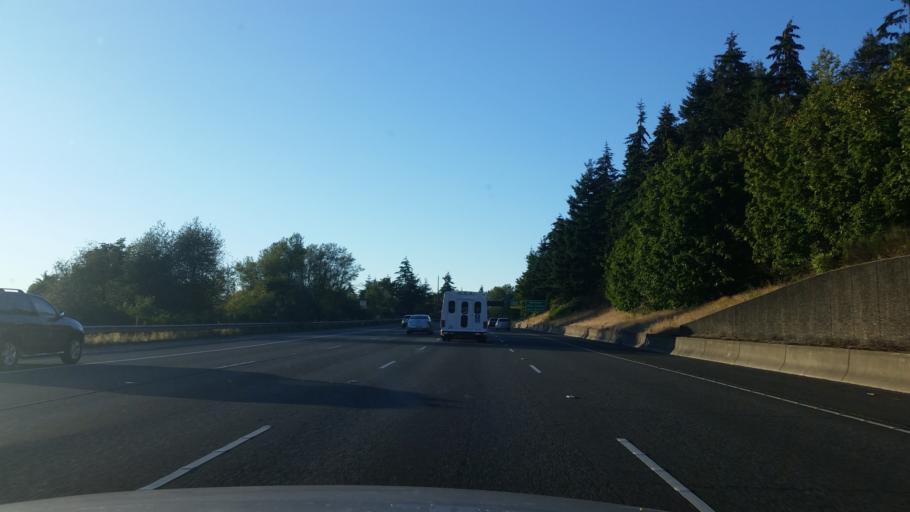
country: US
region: Washington
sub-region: King County
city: Newport
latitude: 47.5894
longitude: -122.1799
